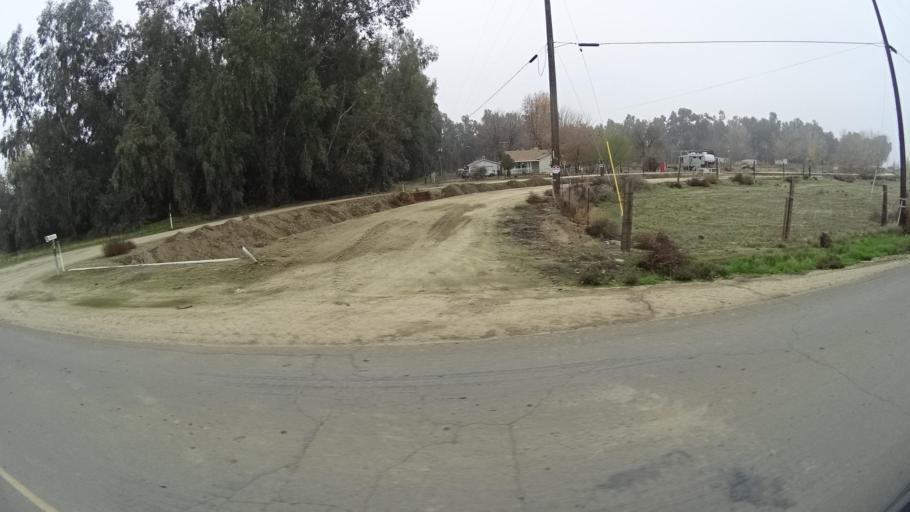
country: US
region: California
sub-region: Kern County
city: Greenfield
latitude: 35.2384
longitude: -119.0876
